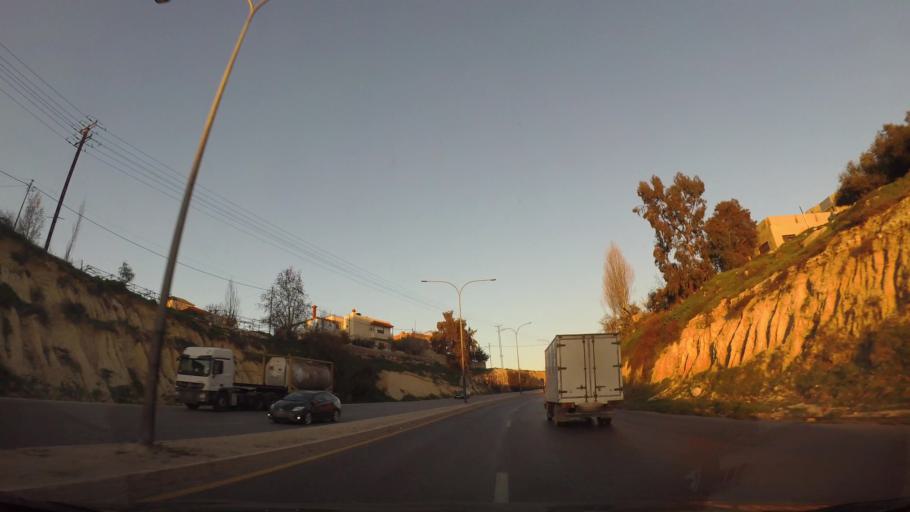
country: JO
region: Amman
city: Umm as Summaq
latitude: 31.8633
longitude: 35.8185
